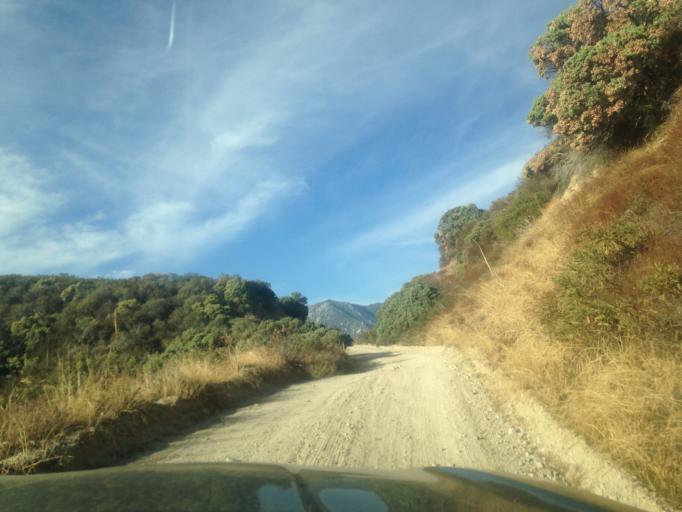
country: US
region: California
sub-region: San Bernardino County
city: Yucaipa
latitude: 34.1226
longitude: -117.0344
